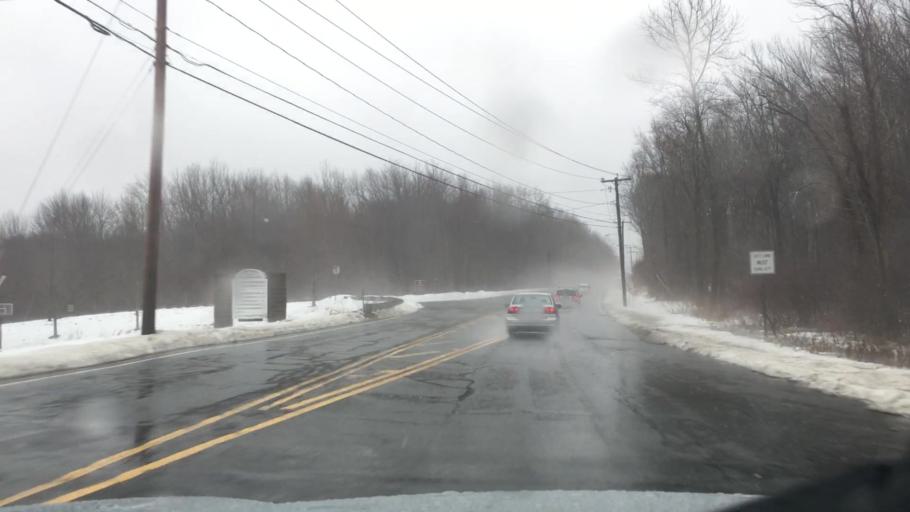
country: US
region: Massachusetts
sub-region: Hampden County
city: Ludlow
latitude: 42.1958
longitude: -72.4984
